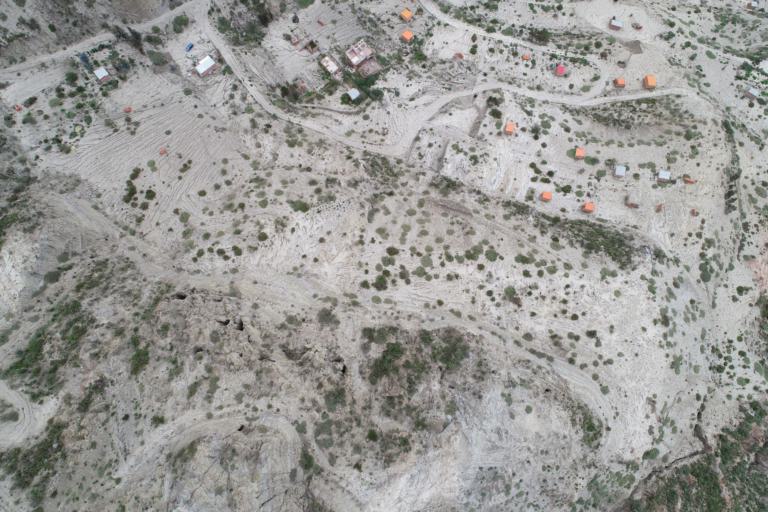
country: BO
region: La Paz
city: La Paz
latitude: -16.5427
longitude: -68.1163
